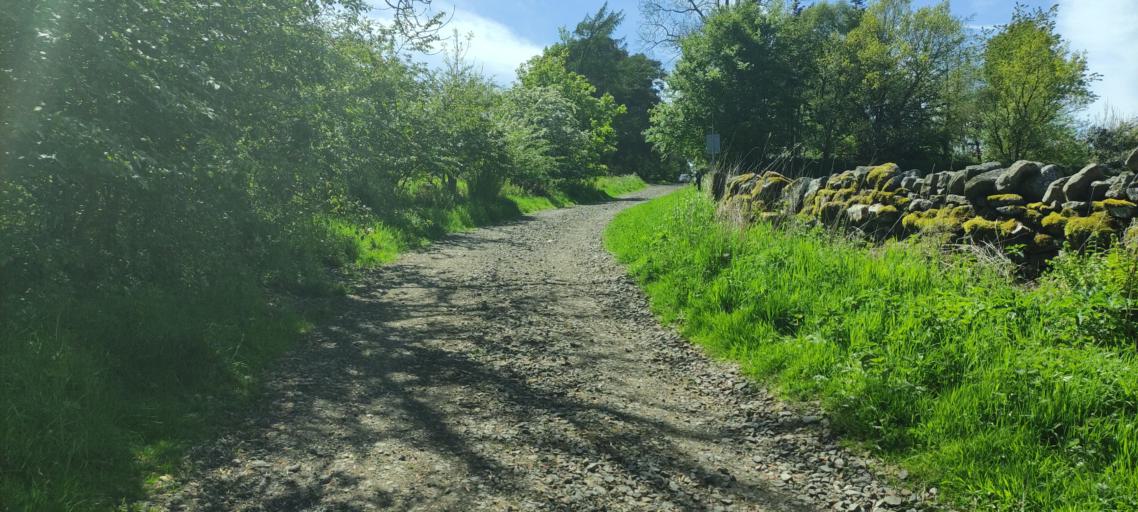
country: GB
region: England
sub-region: Cumbria
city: Brampton
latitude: 54.8932
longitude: -2.6903
